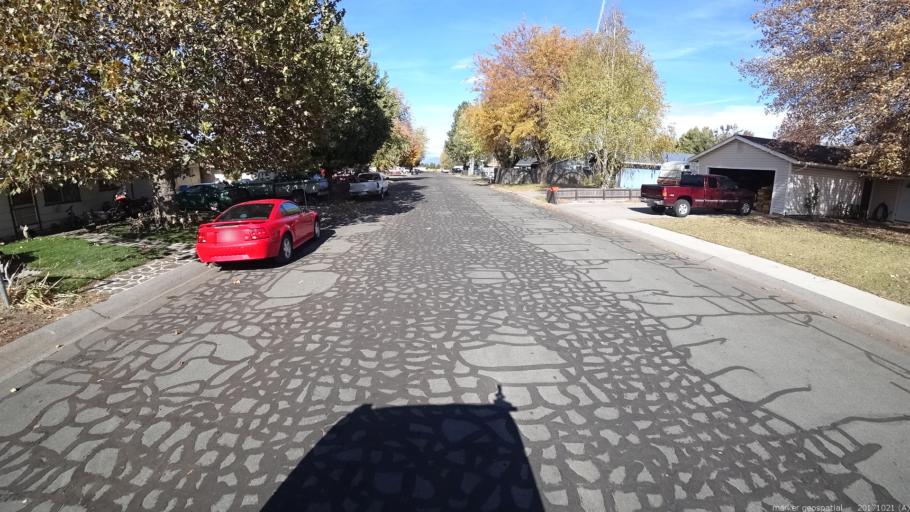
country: US
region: California
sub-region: Shasta County
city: Burney
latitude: 40.8863
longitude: -121.6618
